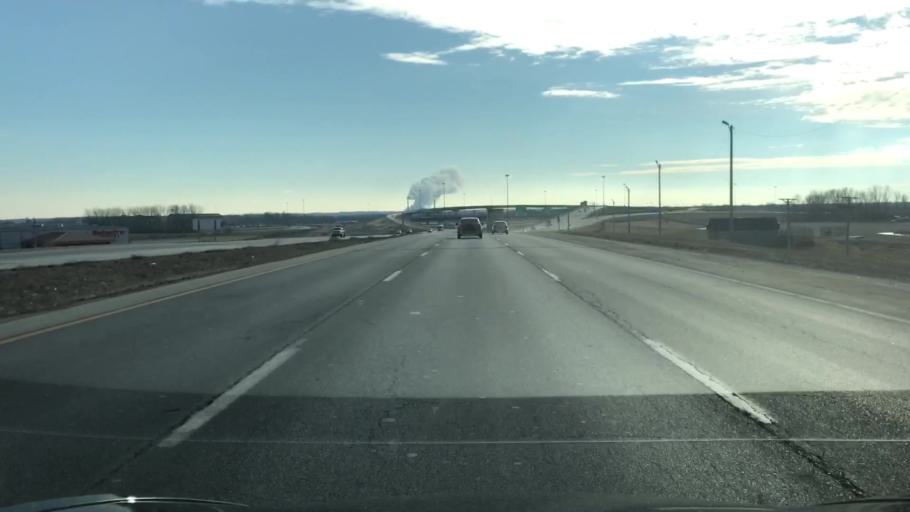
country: US
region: Nebraska
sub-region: Douglas County
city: Omaha
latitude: 41.2413
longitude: -95.9043
